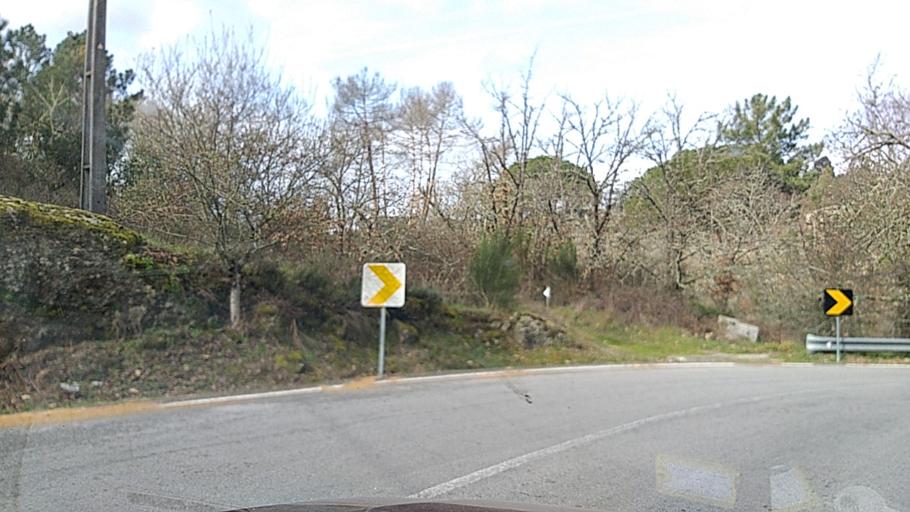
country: PT
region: Viseu
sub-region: Satao
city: Satao
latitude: 40.6655
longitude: -7.6809
